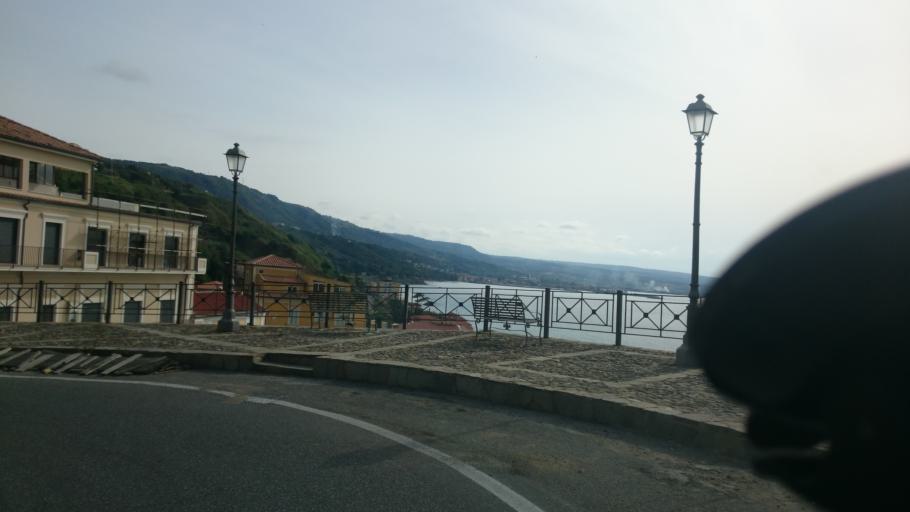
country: IT
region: Calabria
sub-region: Provincia di Vibo-Valentia
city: Maierato
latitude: 38.7354
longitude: 16.1605
